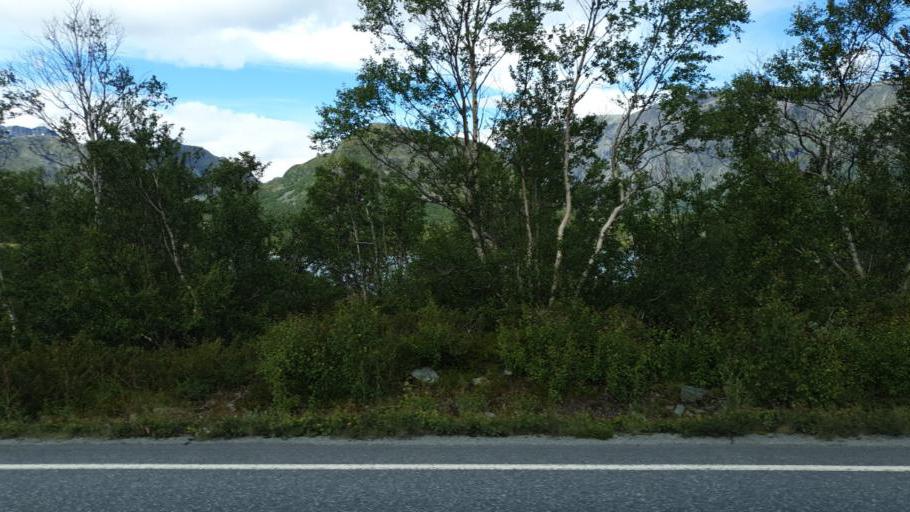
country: NO
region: Oppland
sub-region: Oystre Slidre
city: Heggenes
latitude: 61.4821
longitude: 8.8364
